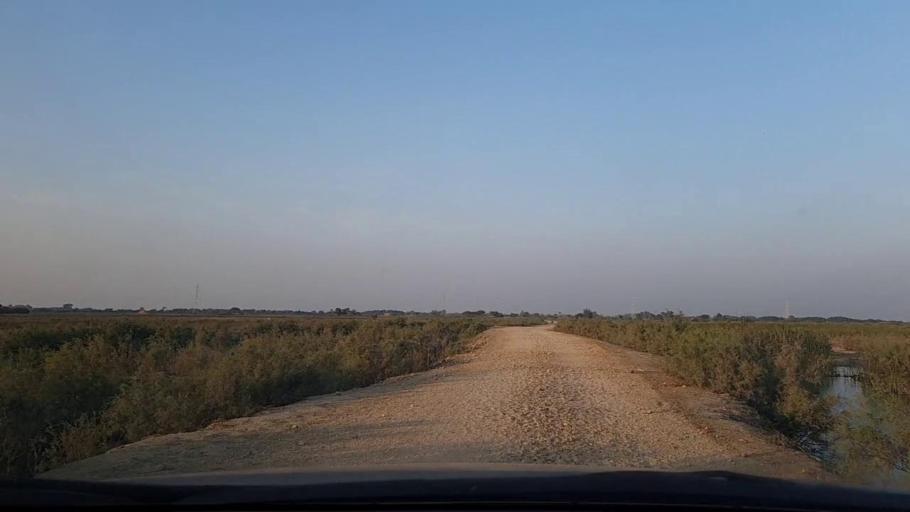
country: PK
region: Sindh
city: Mirpur Sakro
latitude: 24.5552
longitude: 67.6568
